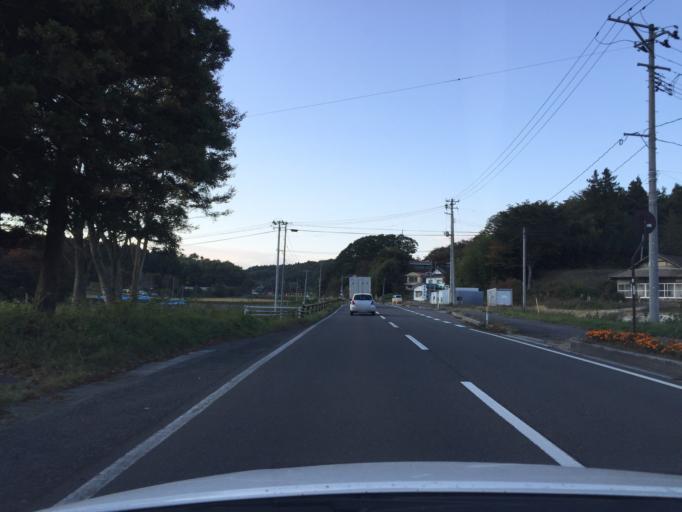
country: JP
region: Fukushima
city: Ishikawa
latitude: 37.2649
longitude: 140.5553
